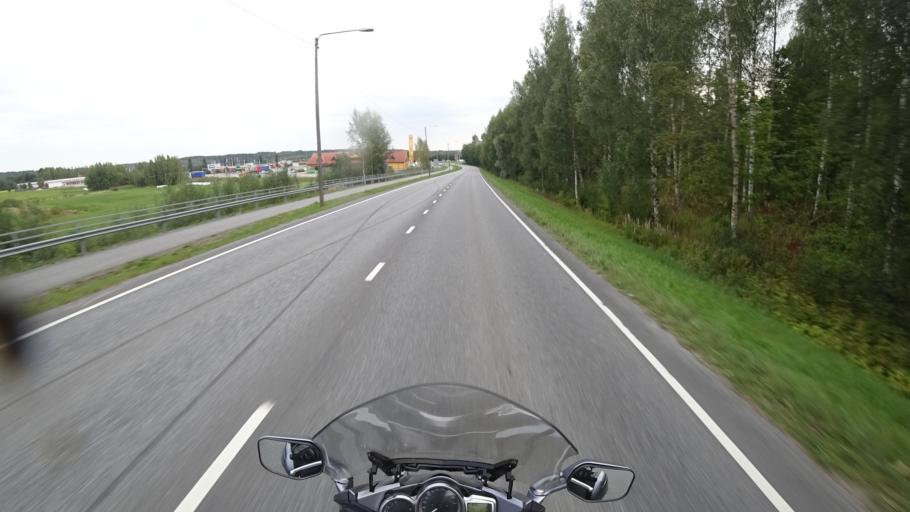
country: FI
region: Uusimaa
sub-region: Raaseporin
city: Karis
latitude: 60.0569
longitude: 23.6446
